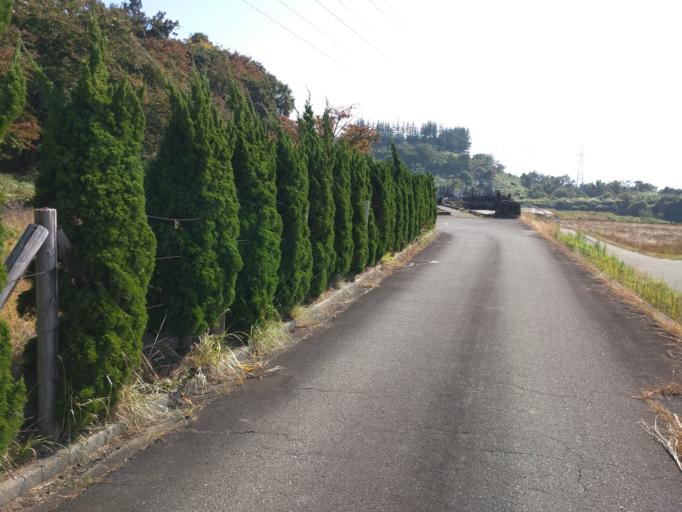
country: JP
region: Fukushima
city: Kitakata
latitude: 37.5314
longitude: 139.9526
